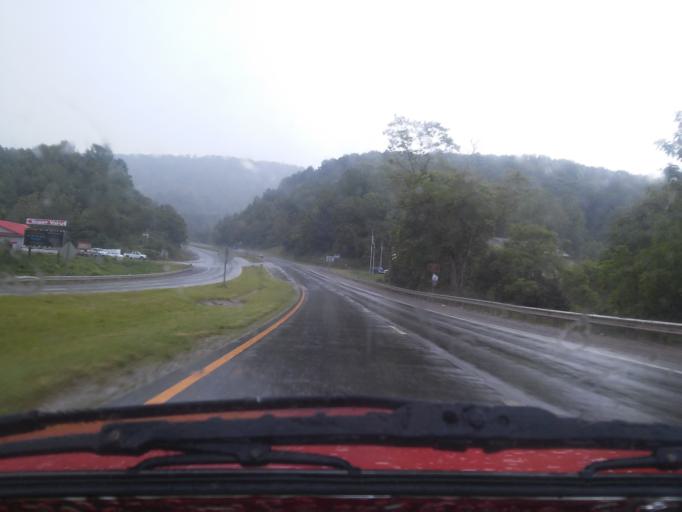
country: US
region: Virginia
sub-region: Montgomery County
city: Prices Fork
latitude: 37.2910
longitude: -80.5001
